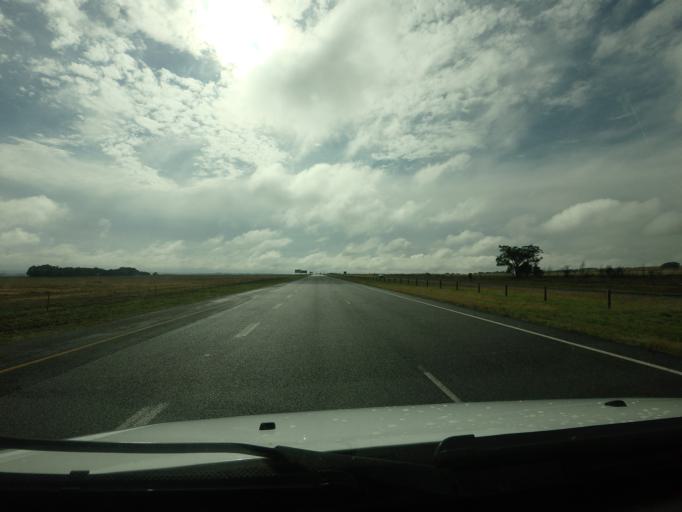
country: ZA
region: Gauteng
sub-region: City of Tshwane Metropolitan Municipality
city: Cullinan
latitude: -25.7975
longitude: 28.5254
